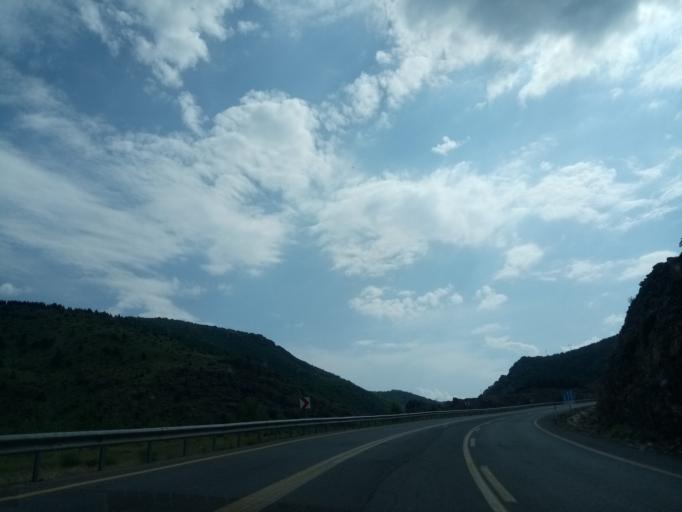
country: TR
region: Konya
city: Aksehir
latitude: 38.2910
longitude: 31.4459
